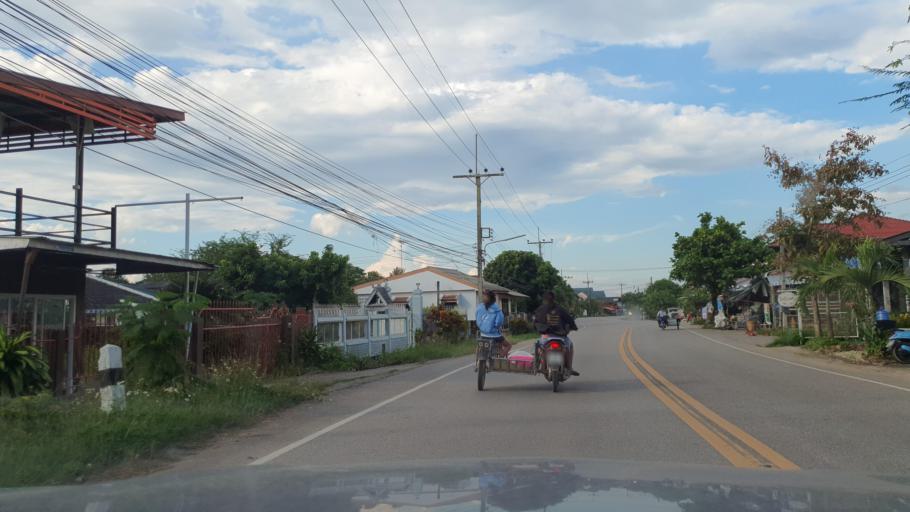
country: TH
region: Phayao
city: Phayao
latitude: 19.1608
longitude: 99.8323
